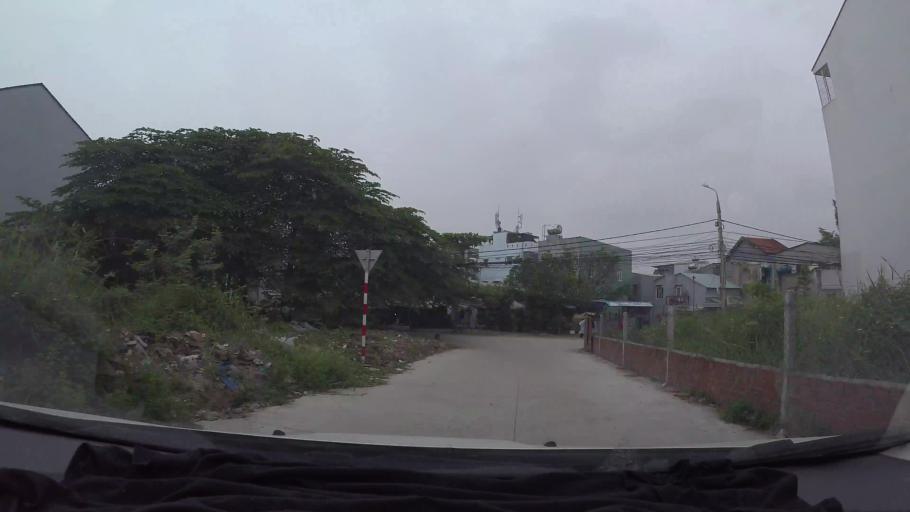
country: VN
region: Da Nang
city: Cam Le
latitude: 16.0284
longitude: 108.2248
